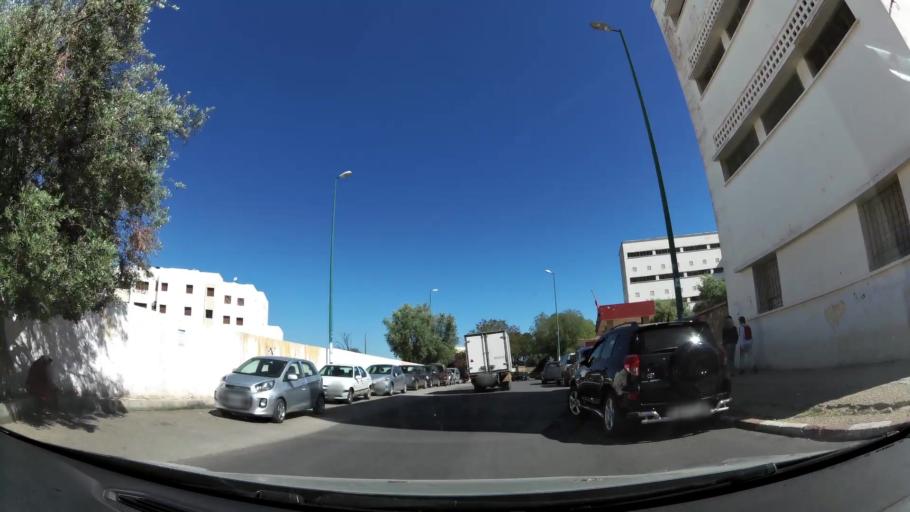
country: MA
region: Meknes-Tafilalet
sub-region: Meknes
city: Meknes
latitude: 33.9035
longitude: -5.5466
